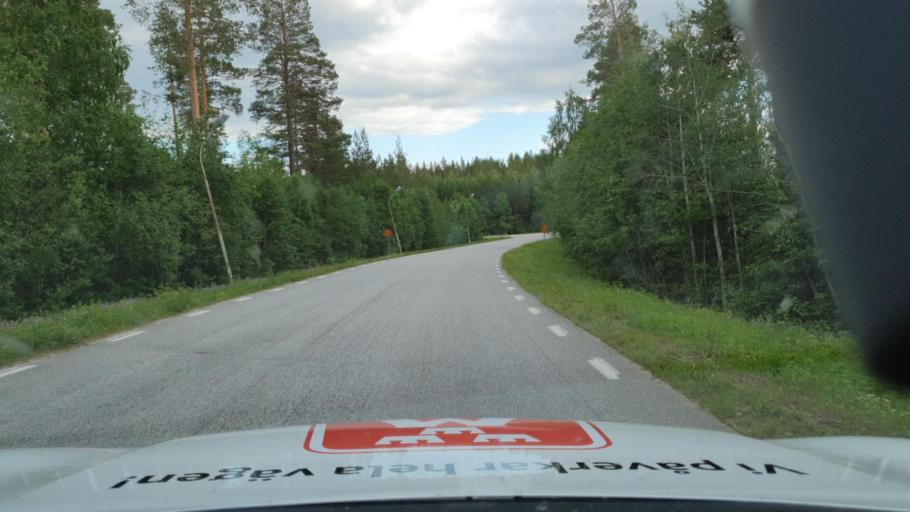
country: SE
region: Vaesterbotten
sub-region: Vindelns Kommun
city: Vindeln
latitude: 64.3144
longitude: 19.6289
